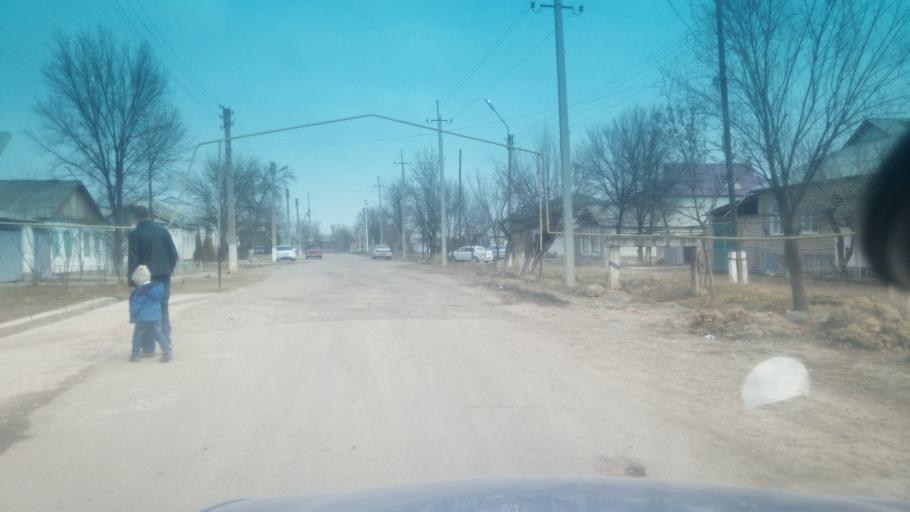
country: UZ
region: Sirdaryo
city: Guliston
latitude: 40.4946
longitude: 68.7830
